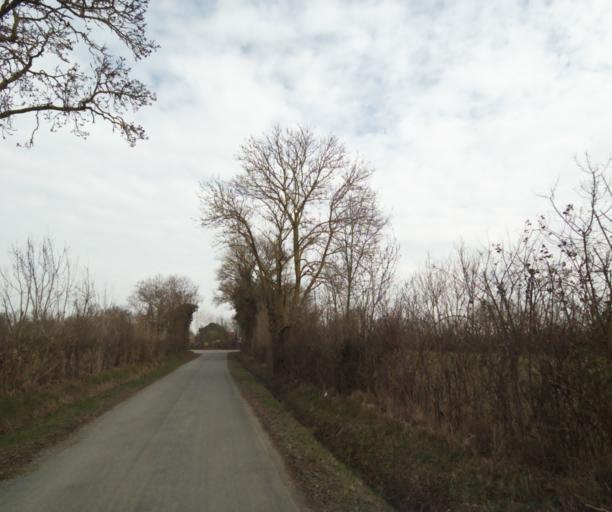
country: FR
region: Poitou-Charentes
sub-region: Departement des Deux-Sevres
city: Niort
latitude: 46.2933
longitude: -0.4727
